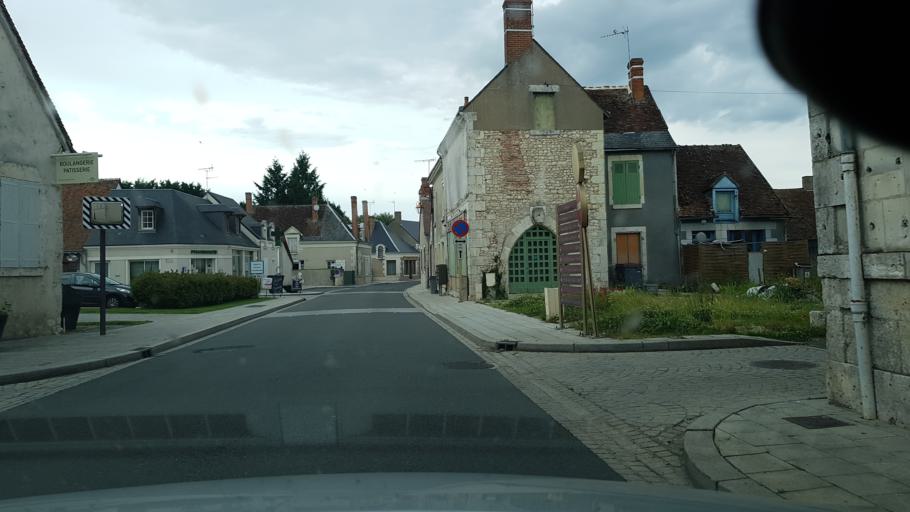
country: FR
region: Centre
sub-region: Departement du Loir-et-Cher
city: Chatillon-sur-Cher
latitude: 47.3448
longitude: 1.4790
